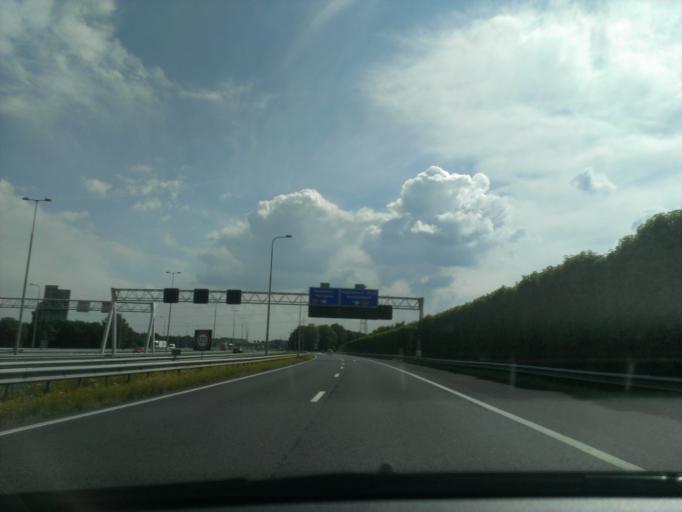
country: NL
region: Gelderland
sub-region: Gemeente Apeldoorn
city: Apeldoorn
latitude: 52.1942
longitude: 6.0190
